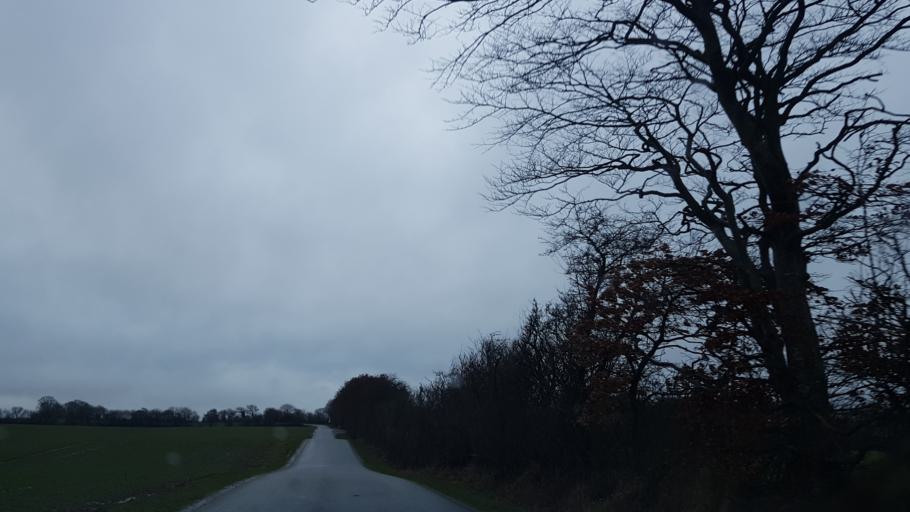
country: DK
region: South Denmark
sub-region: Kolding Kommune
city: Vamdrup
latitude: 55.3889
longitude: 9.3082
